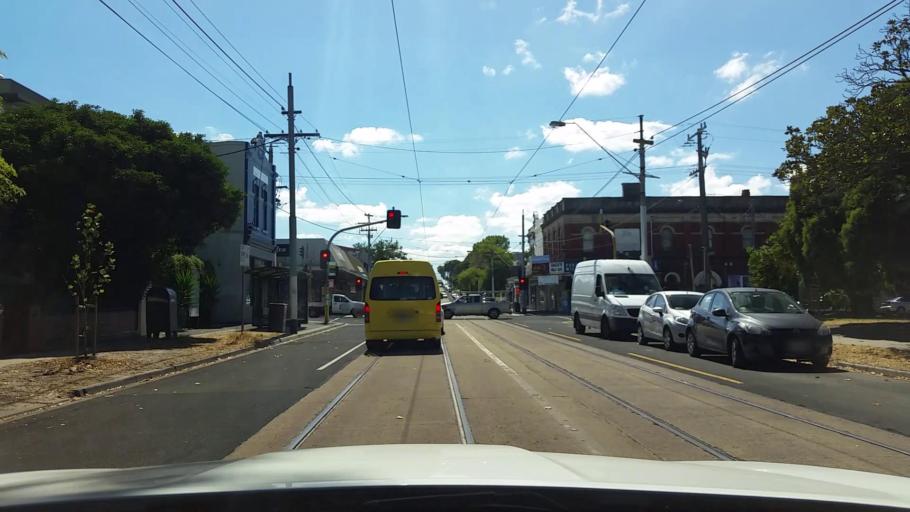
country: AU
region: Victoria
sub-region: Glen Eira
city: Caulfield North
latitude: -37.8701
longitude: 145.0252
